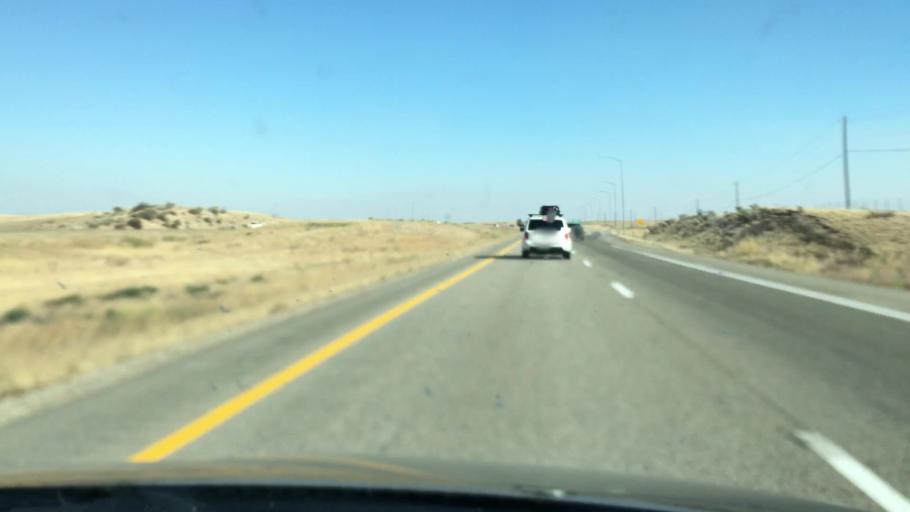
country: US
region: Idaho
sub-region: Ada County
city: Boise
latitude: 43.4389
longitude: -116.0667
